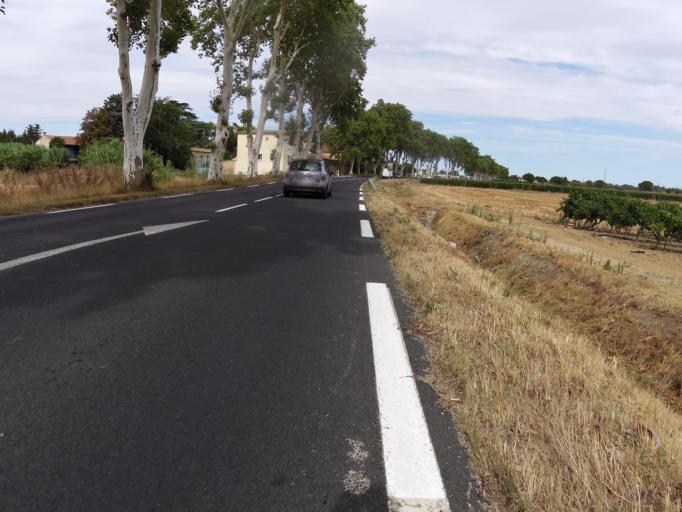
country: FR
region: Languedoc-Roussillon
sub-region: Departement du Gard
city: Mus
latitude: 43.7177
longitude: 4.2032
